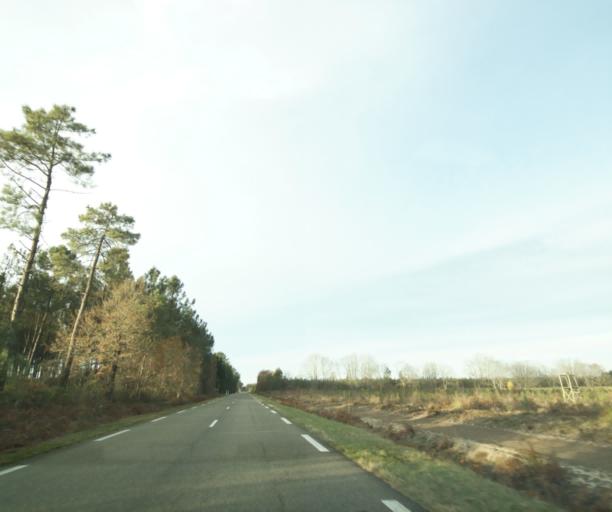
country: FR
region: Aquitaine
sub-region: Departement des Landes
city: Gabarret
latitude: 44.0252
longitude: -0.0261
